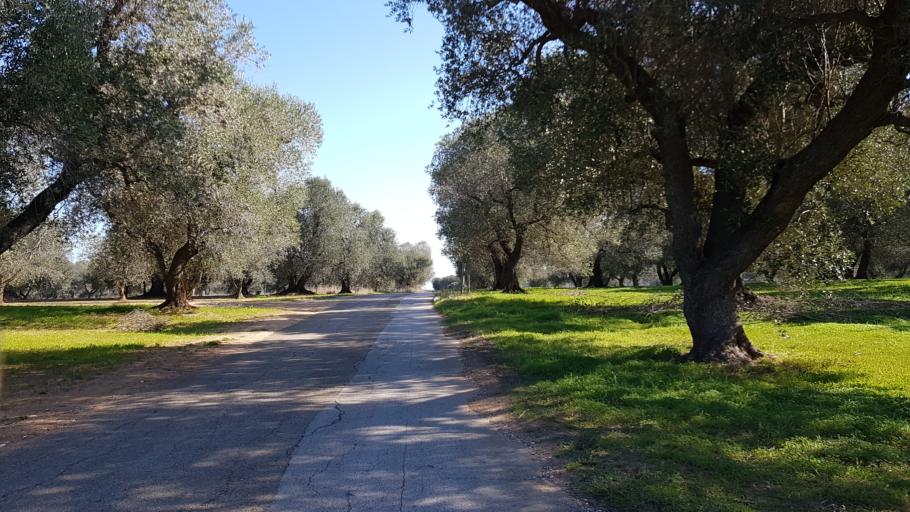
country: IT
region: Apulia
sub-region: Provincia di Brindisi
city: Mesagne
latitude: 40.6194
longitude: 17.8359
